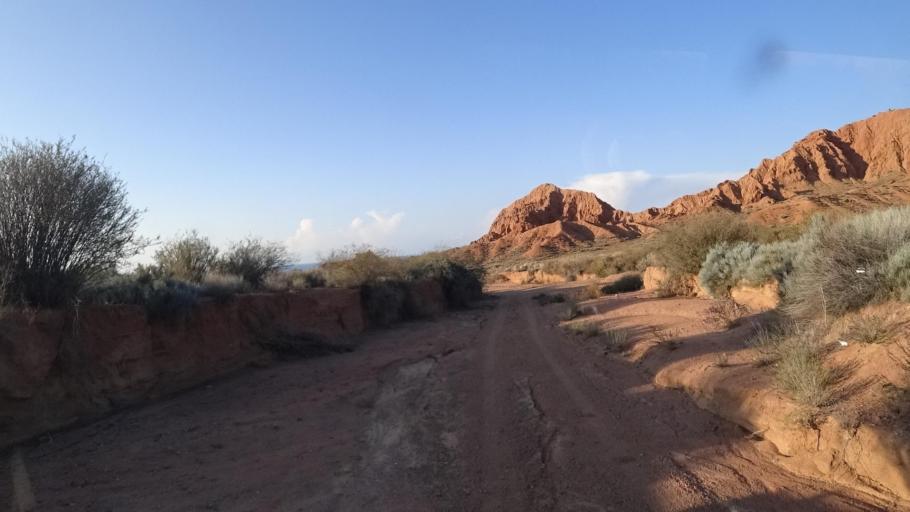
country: KG
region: Ysyk-Koel
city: Kadzhi-Say
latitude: 42.1447
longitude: 77.1482
